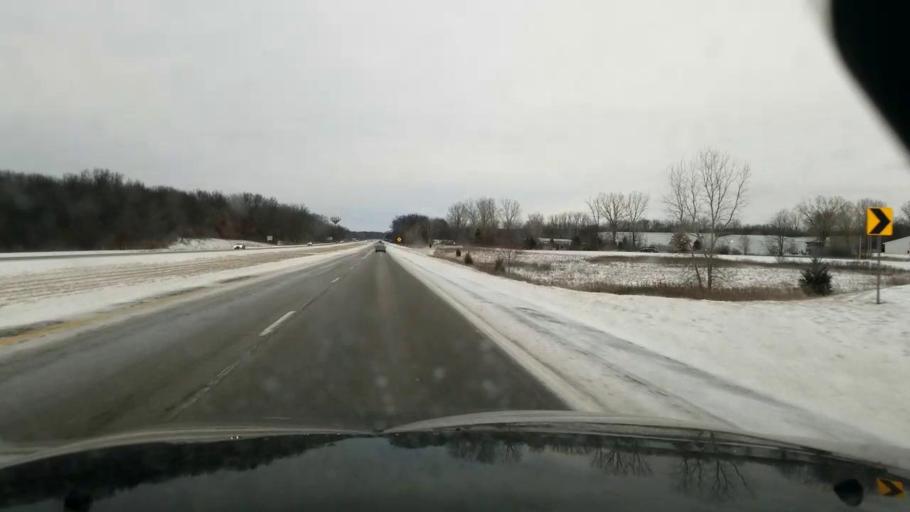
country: US
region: Michigan
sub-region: Jackson County
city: Jackson
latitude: 42.2531
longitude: -84.4764
